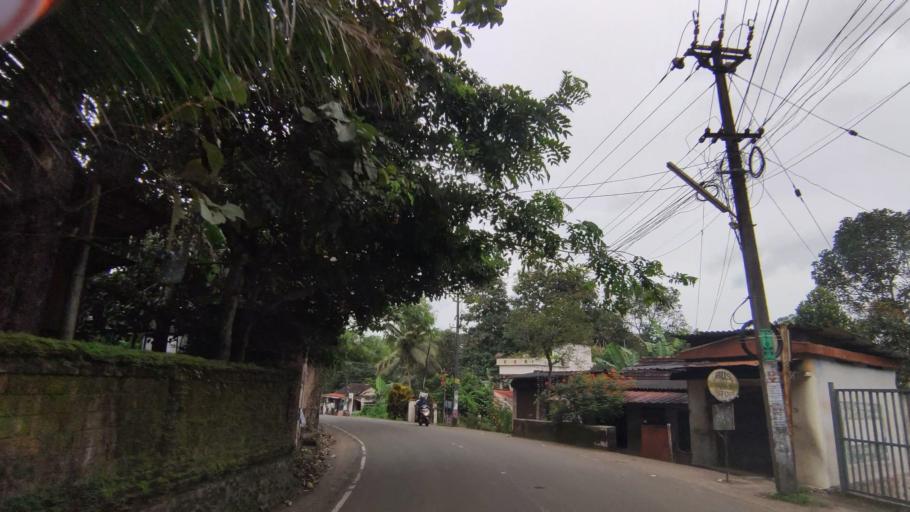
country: IN
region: Kerala
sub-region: Kottayam
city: Kottayam
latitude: 9.6532
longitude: 76.5244
